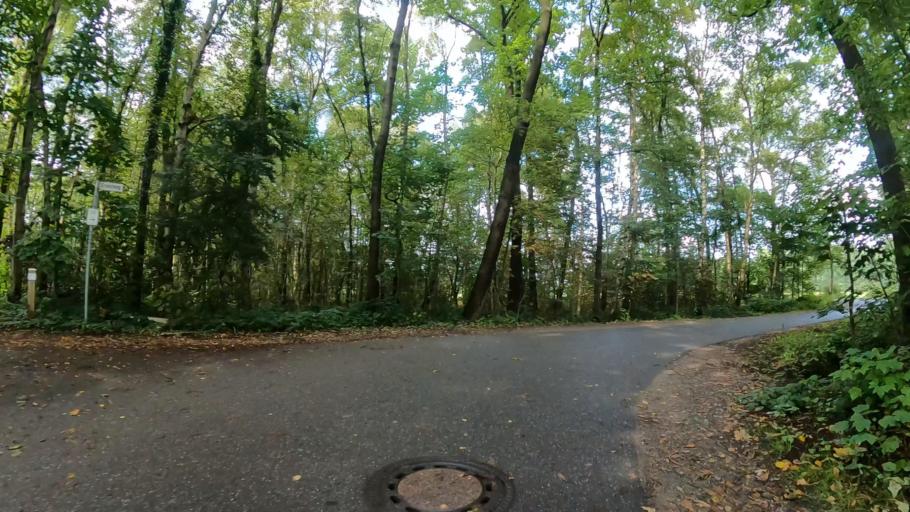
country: DE
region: Schleswig-Holstein
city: Tornesch
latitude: 53.7178
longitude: 9.7064
